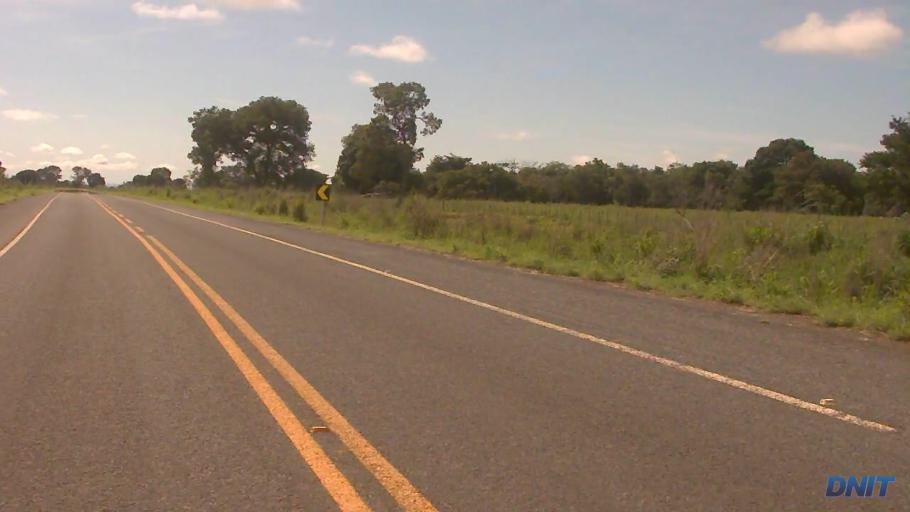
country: BR
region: Goias
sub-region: Sao Miguel Do Araguaia
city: Sao Miguel do Araguaia
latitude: -13.3165
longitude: -50.1672
